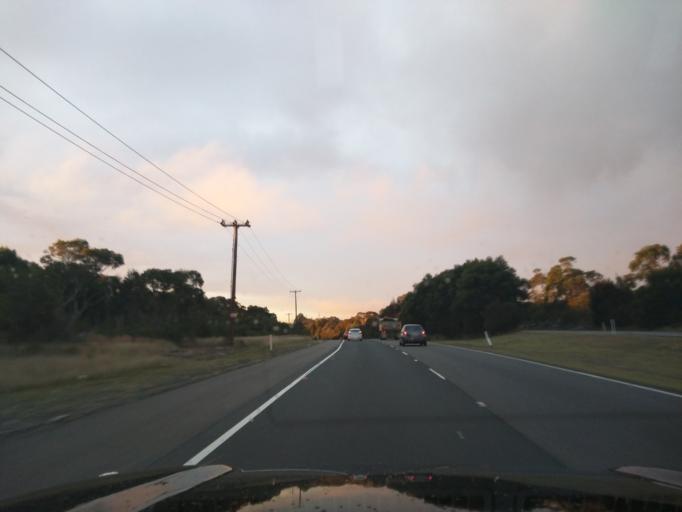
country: AU
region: New South Wales
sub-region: Sutherland Shire
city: Heathcote
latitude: -34.1122
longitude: 150.9925
